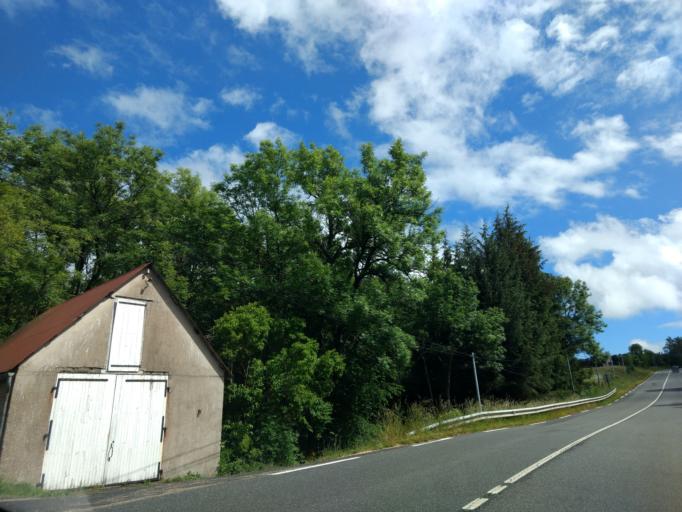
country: FR
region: Midi-Pyrenees
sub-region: Departement de l'Aveyron
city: Laguiole
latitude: 44.6775
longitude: 2.8512
